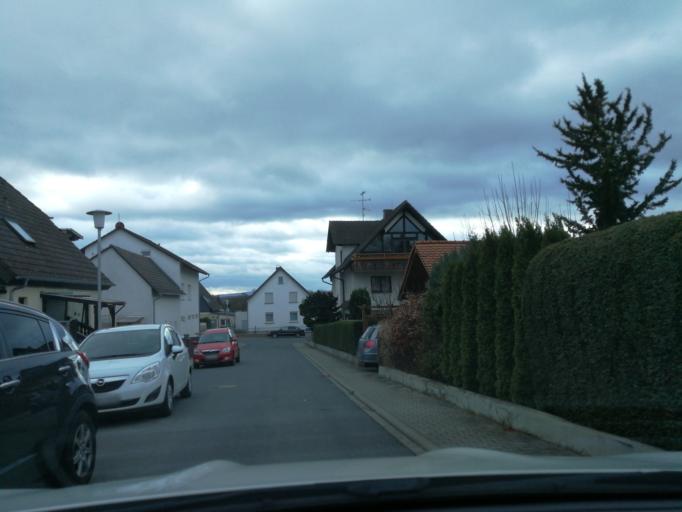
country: DE
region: Hesse
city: Reinheim
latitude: 49.8470
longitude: 8.8030
